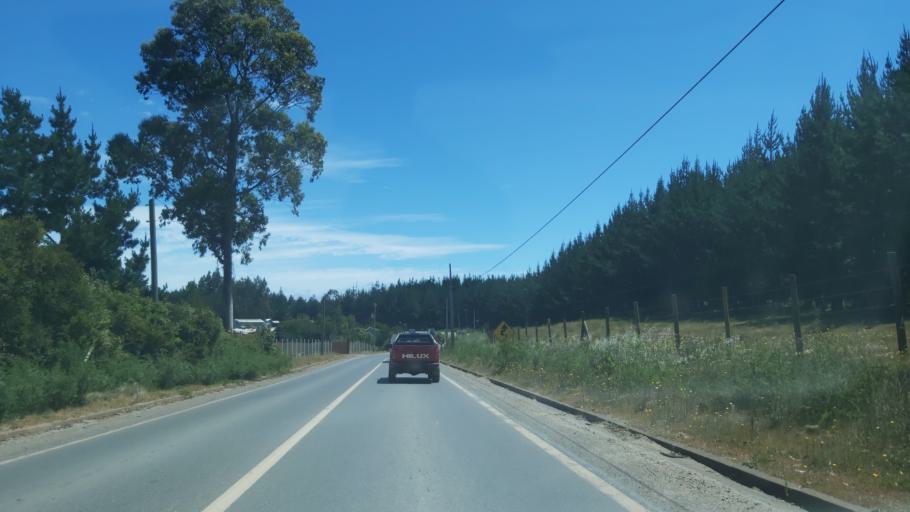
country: CL
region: Maule
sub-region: Provincia de Talca
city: Constitucion
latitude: -35.3978
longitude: -72.4328
